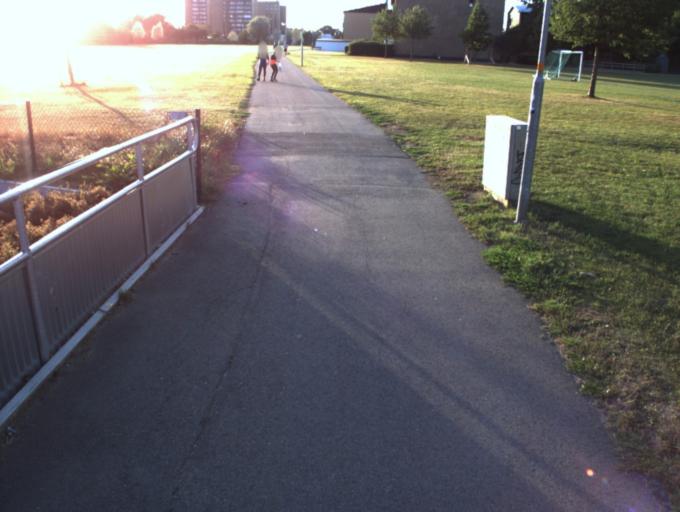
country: SE
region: Skane
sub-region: Helsingborg
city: Helsingborg
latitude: 56.0257
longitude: 12.7301
